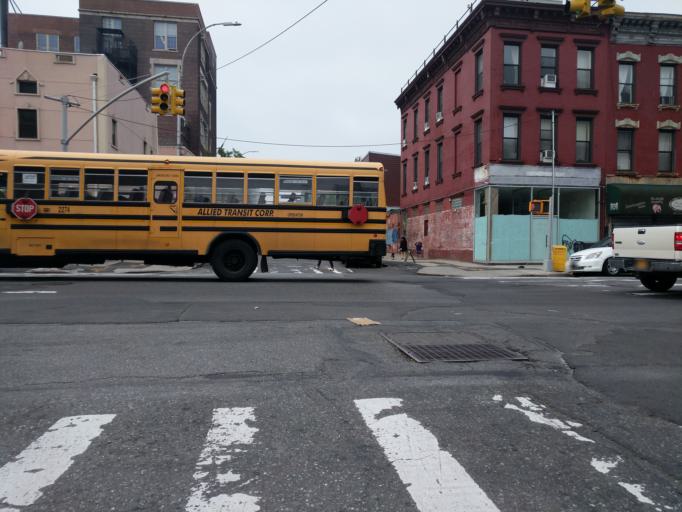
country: US
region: New York
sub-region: Queens County
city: Long Island City
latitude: 40.7115
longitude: -73.9473
